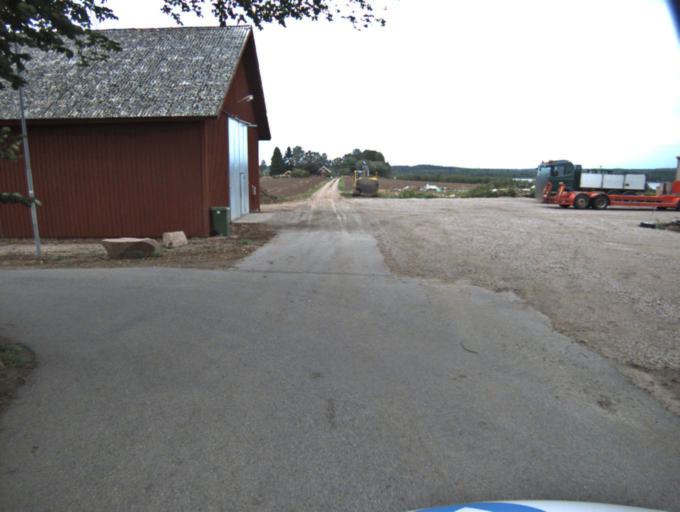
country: SE
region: Vaestra Goetaland
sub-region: Ulricehamns Kommun
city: Ulricehamn
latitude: 57.8393
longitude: 13.2939
